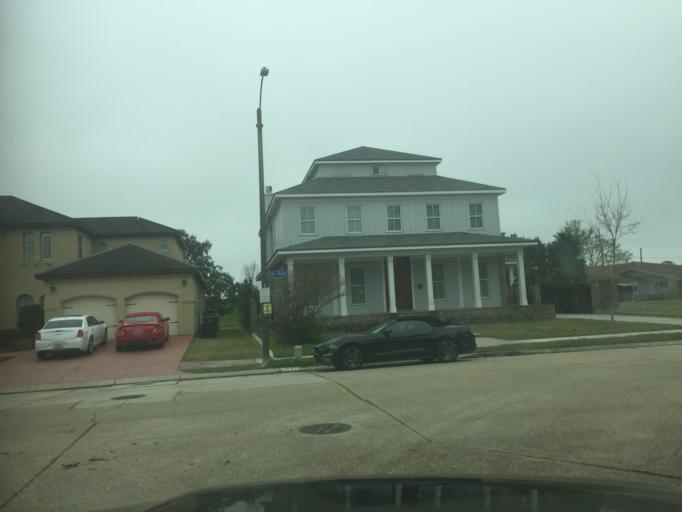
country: US
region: Louisiana
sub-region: Jefferson Parish
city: Metairie
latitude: 30.0199
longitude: -90.0998
